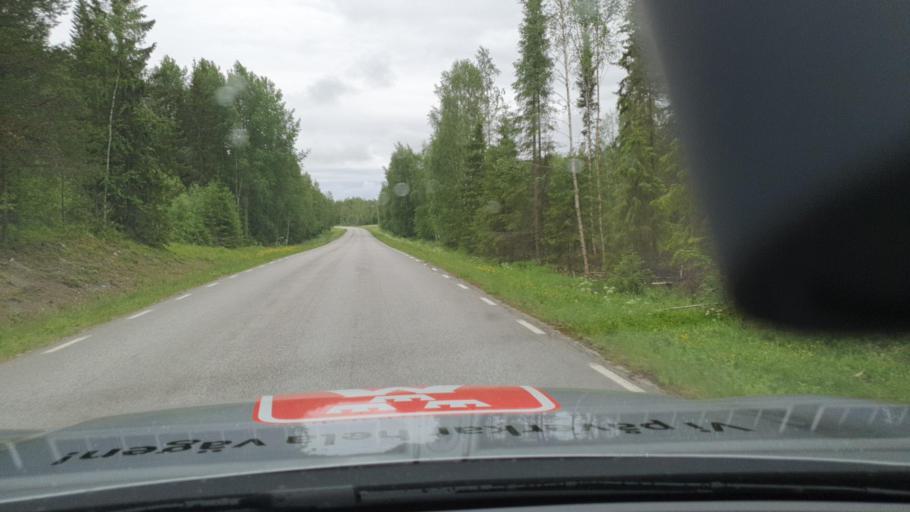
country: SE
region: Norrbotten
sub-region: Kalix Kommun
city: Toere
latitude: 65.8640
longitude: 22.6762
